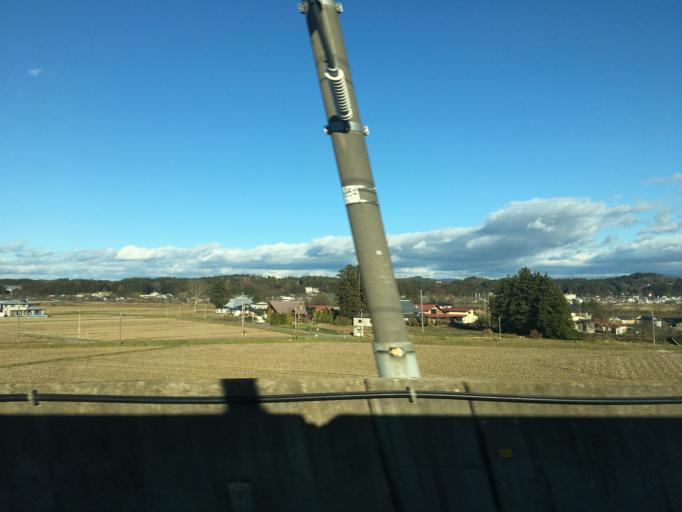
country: JP
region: Iwate
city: Mizusawa
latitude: 39.1947
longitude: 141.1572
